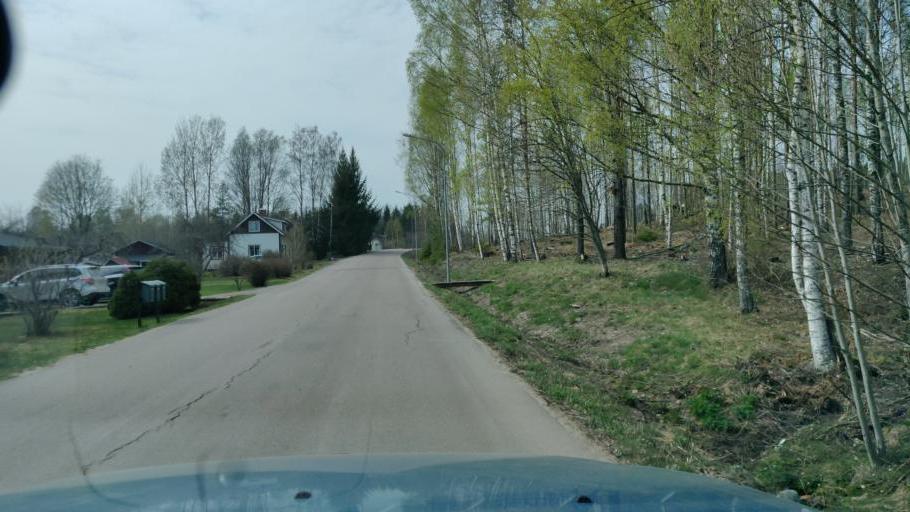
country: SE
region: Vaermland
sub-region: Munkfors Kommun
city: Munkfors
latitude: 59.8349
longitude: 13.5138
